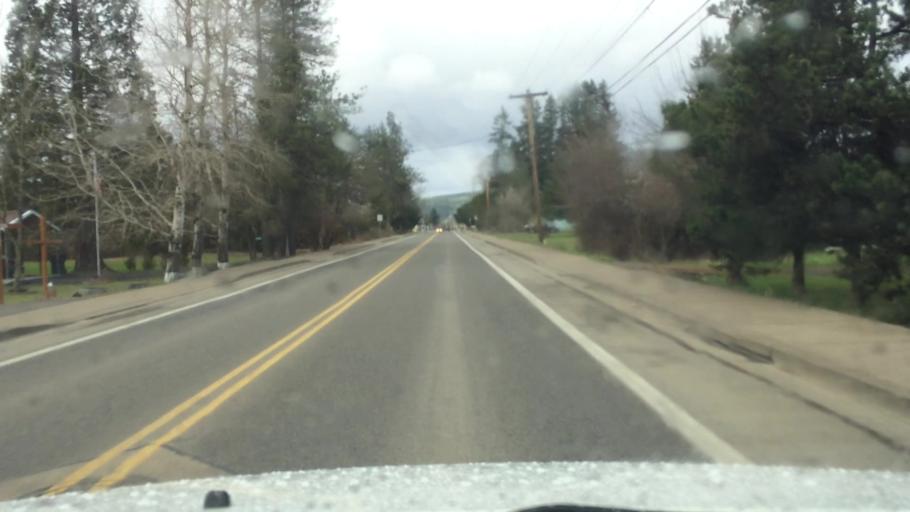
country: US
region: Oregon
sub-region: Polk County
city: Grand Ronde
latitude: 45.0703
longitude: -123.6119
